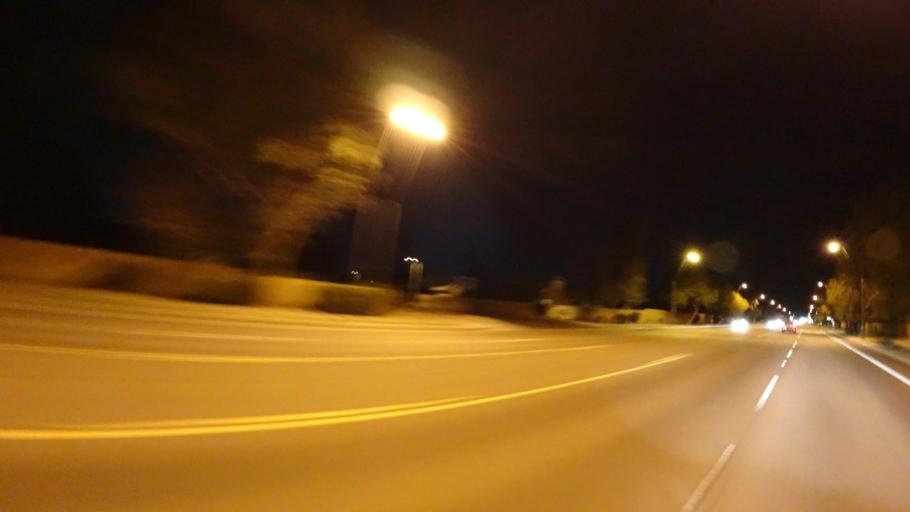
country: US
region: Arizona
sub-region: Maricopa County
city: San Carlos
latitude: 33.3346
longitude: -111.9046
